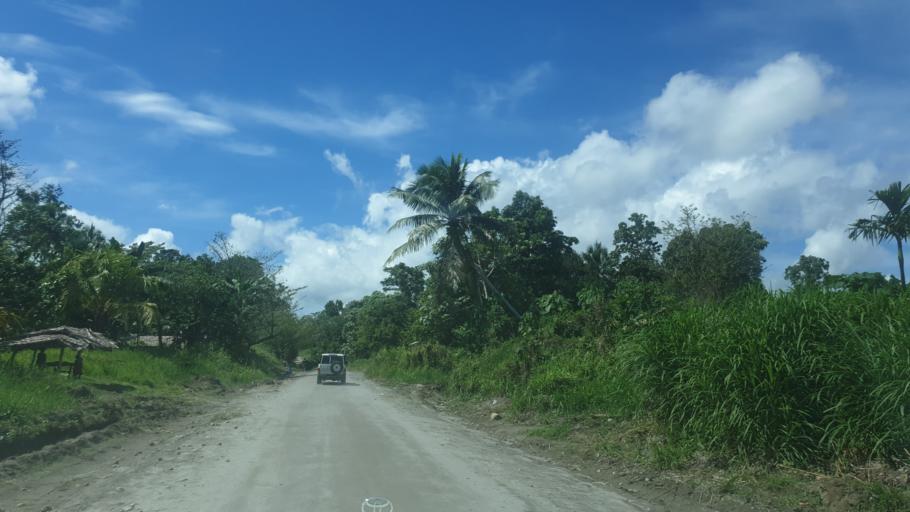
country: PG
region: Bougainville
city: Panguna
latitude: -6.6604
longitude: 155.4479
